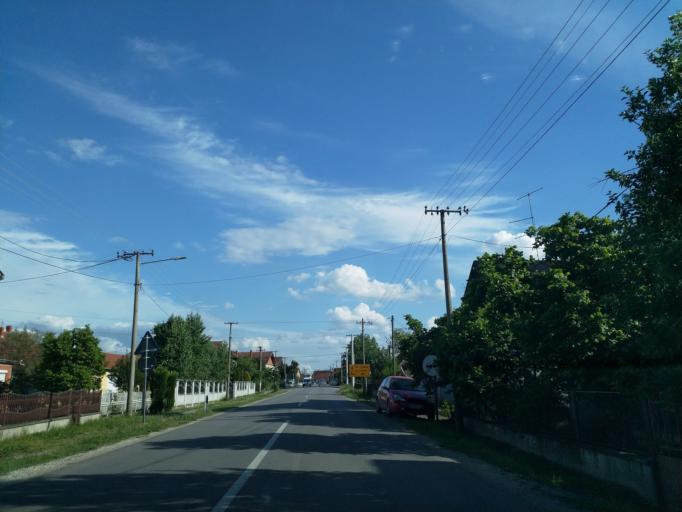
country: RS
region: Central Serbia
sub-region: Sumadijski Okrug
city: Lapovo
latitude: 44.1875
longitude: 21.0910
